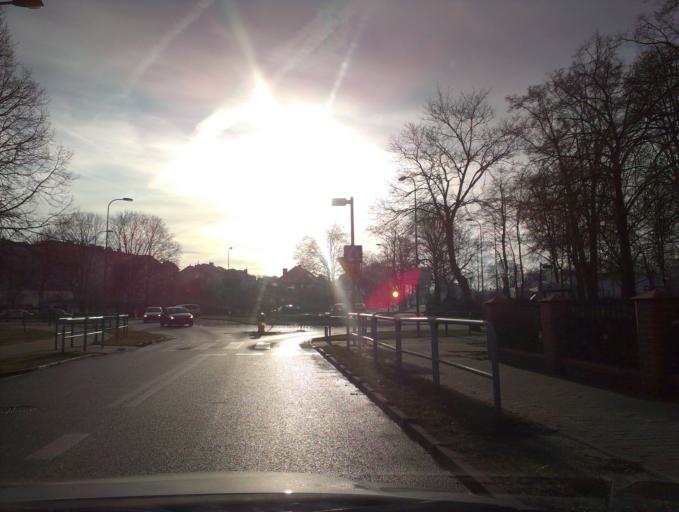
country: PL
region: West Pomeranian Voivodeship
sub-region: Powiat szczecinecki
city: Szczecinek
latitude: 53.6985
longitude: 16.6985
